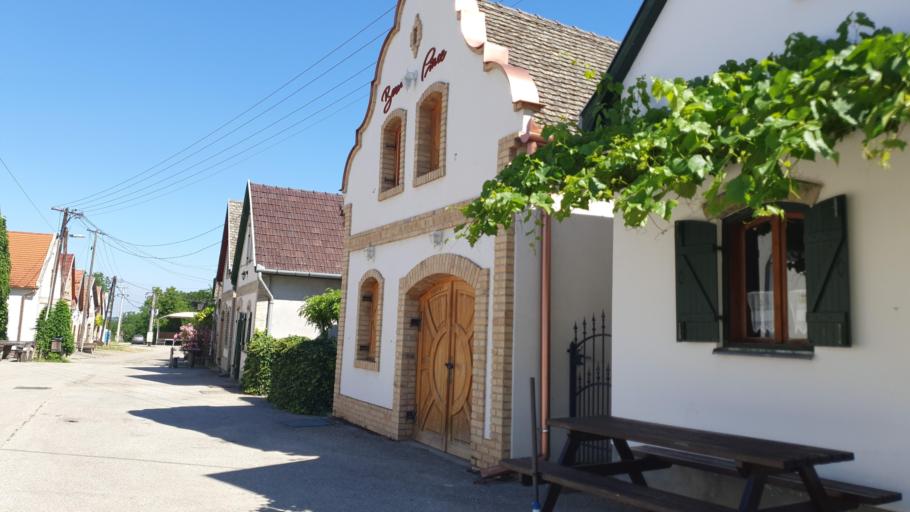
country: HU
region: Bacs-Kiskun
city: Hajos
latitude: 46.3854
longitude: 19.1498
